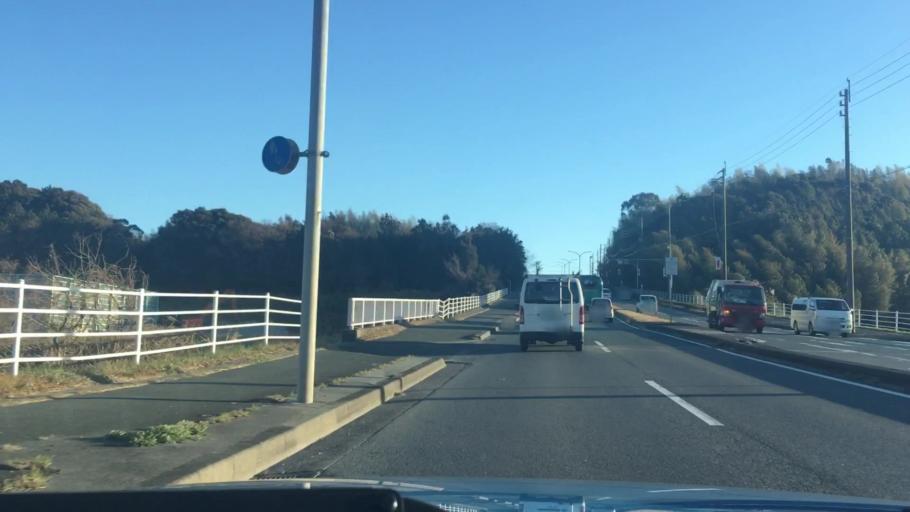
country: JP
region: Shizuoka
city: Hamamatsu
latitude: 34.7456
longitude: 137.6656
